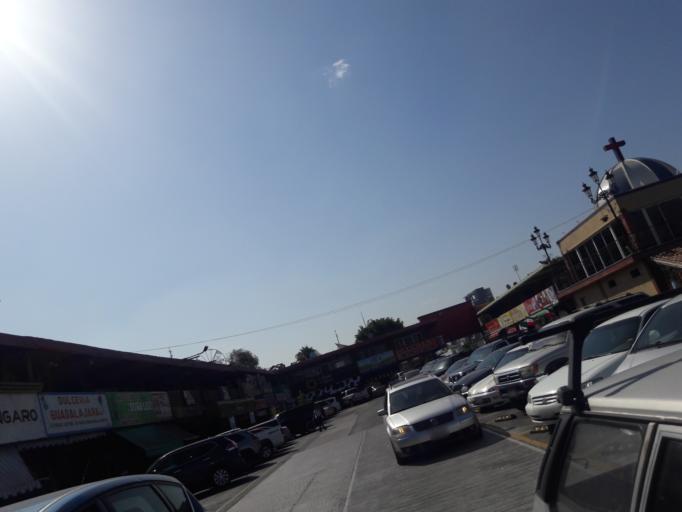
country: MX
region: Baja California
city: Tijuana
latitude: 32.5278
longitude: -117.0254
